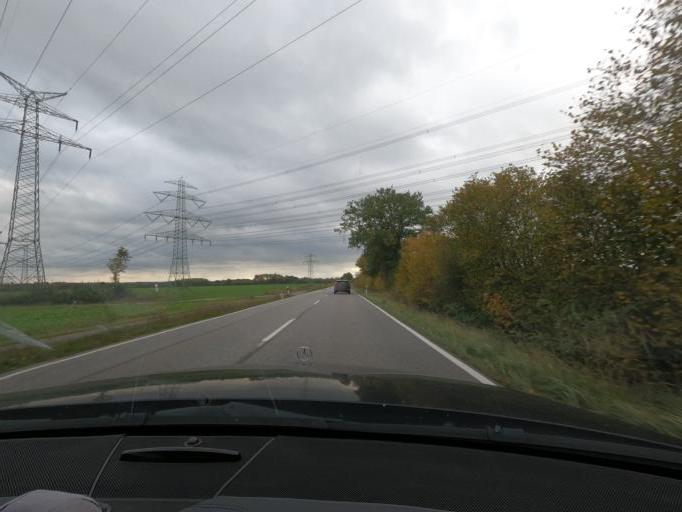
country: DE
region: Schleswig-Holstein
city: Hohenhorn
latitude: 53.4639
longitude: 10.3684
